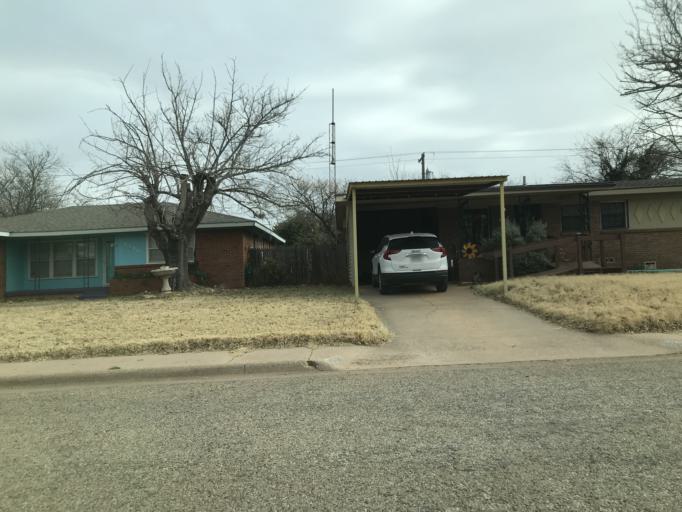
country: US
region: Texas
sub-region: Taylor County
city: Abilene
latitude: 32.4644
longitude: -99.7611
